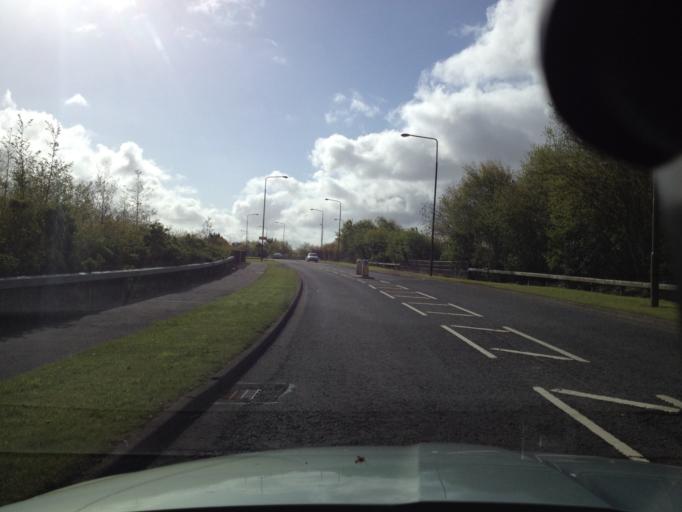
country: GB
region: Scotland
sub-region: West Lothian
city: Livingston
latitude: 55.8703
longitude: -3.5161
